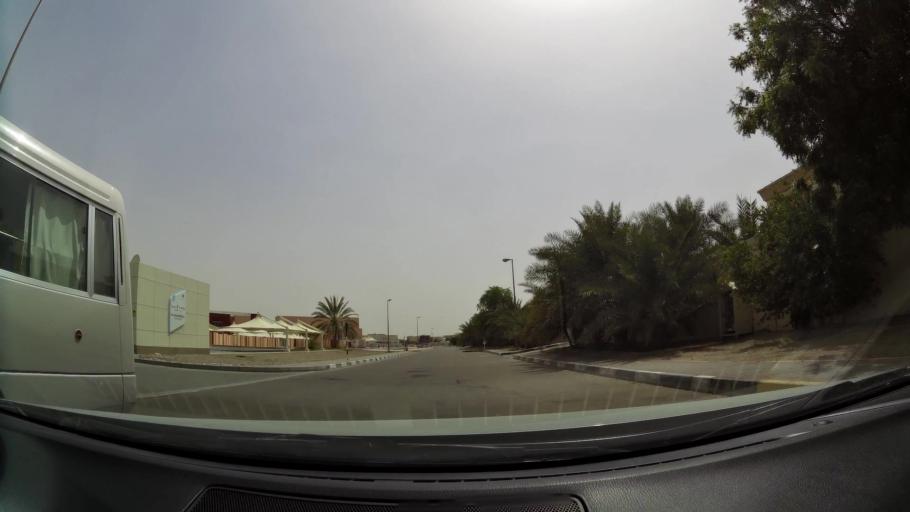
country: AE
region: Abu Dhabi
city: Al Ain
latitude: 24.1618
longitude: 55.6643
